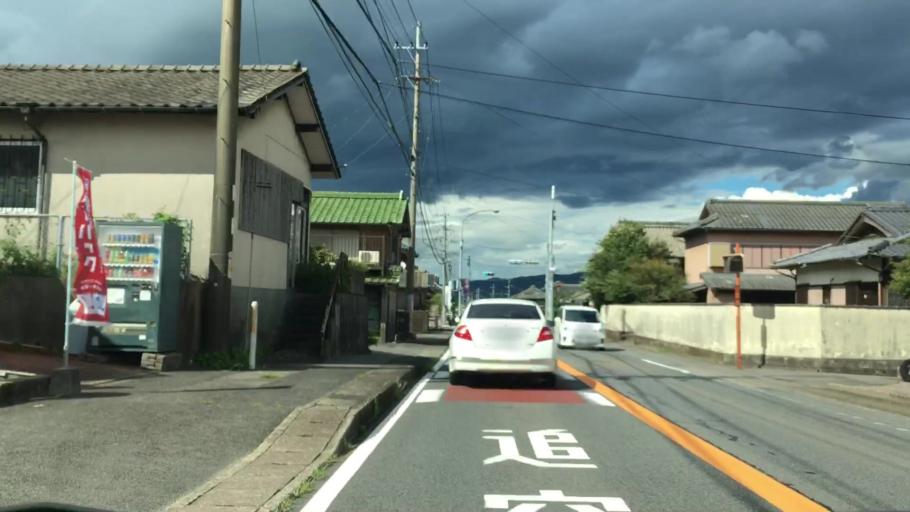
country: JP
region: Saga Prefecture
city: Imaricho-ko
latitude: 33.2448
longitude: 129.8511
